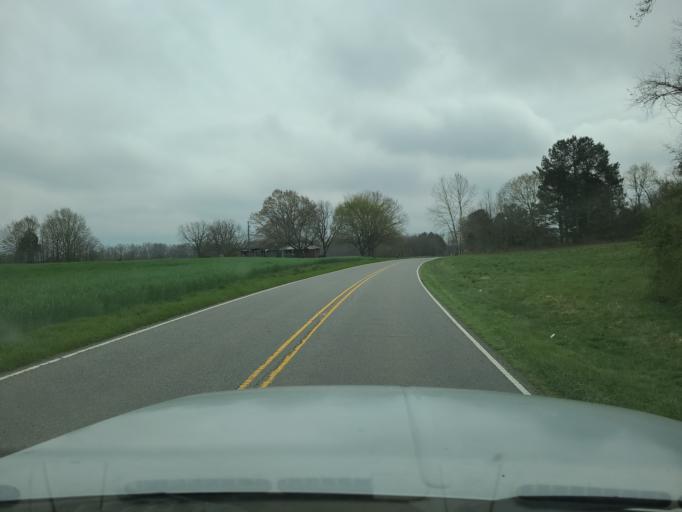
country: US
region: North Carolina
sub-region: Cleveland County
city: Shelby
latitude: 35.3970
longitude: -81.6262
